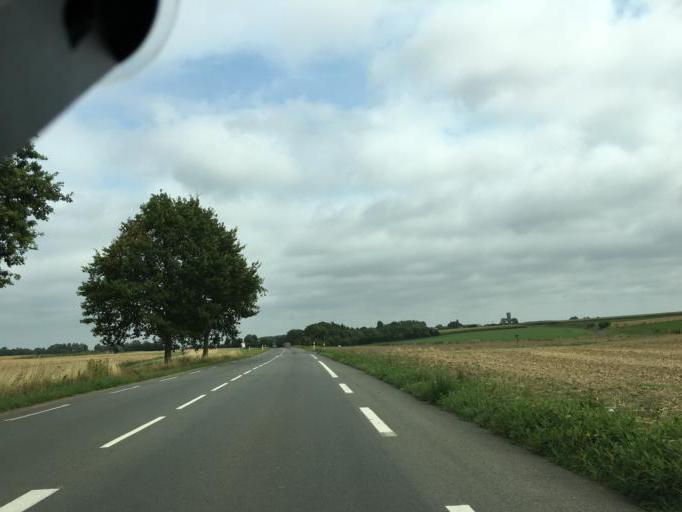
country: FR
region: Nord-Pas-de-Calais
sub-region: Departement du Pas-de-Calais
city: Camblain-Chatelain
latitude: 50.4268
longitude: 2.4354
